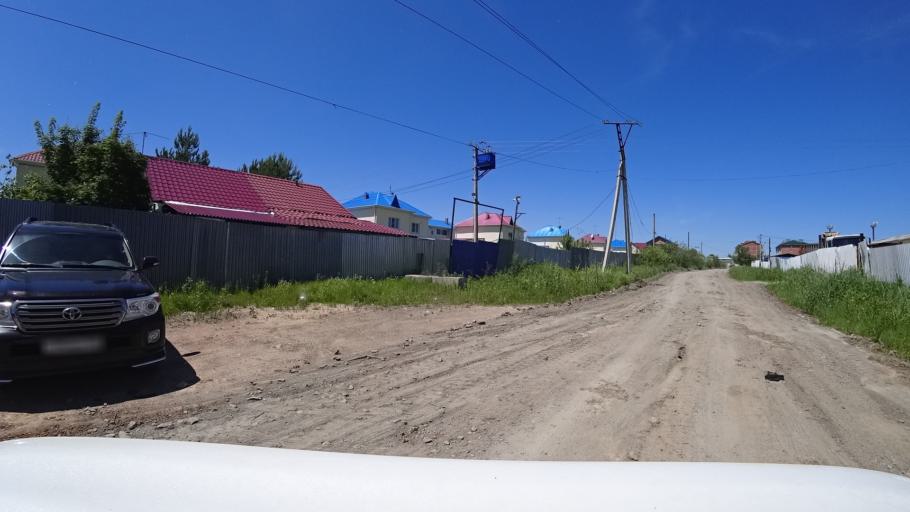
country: RU
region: Khabarovsk Krai
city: Topolevo
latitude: 48.5032
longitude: 135.1793
